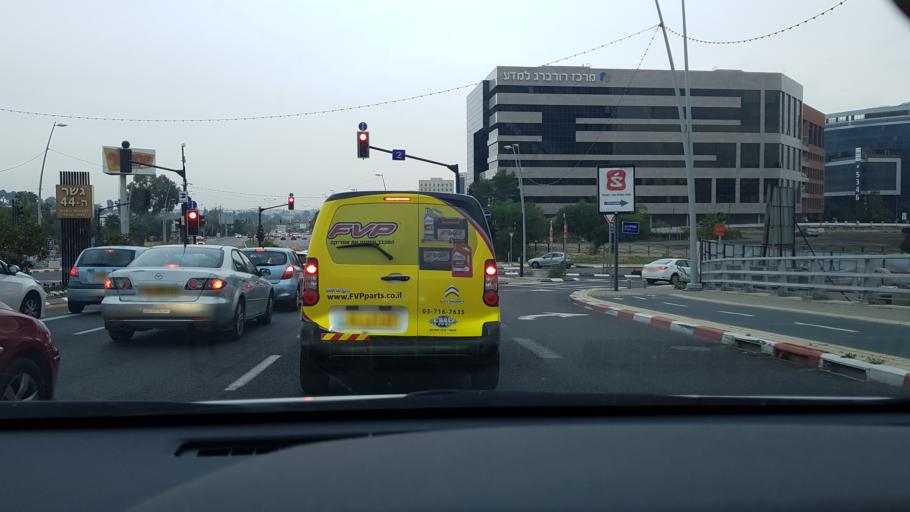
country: IL
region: Central District
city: Ness Ziona
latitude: 31.9096
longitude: 34.8048
